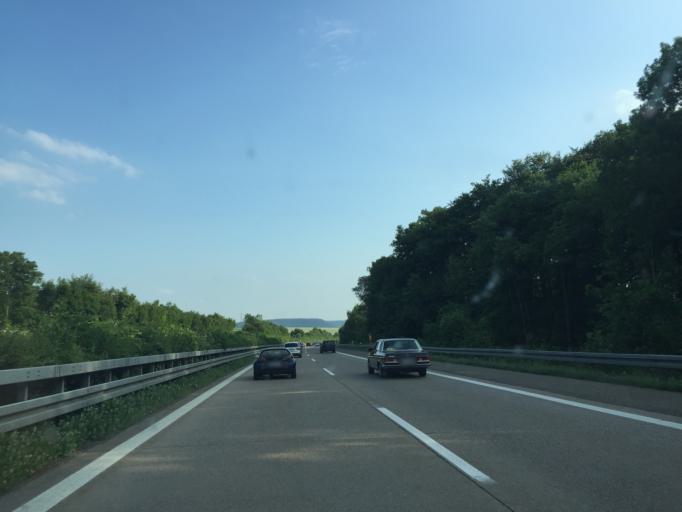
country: DE
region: Baden-Wuerttemberg
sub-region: Regierungsbezirk Stuttgart
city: Neuenstadt am Kocher
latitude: 49.2620
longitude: 9.3533
